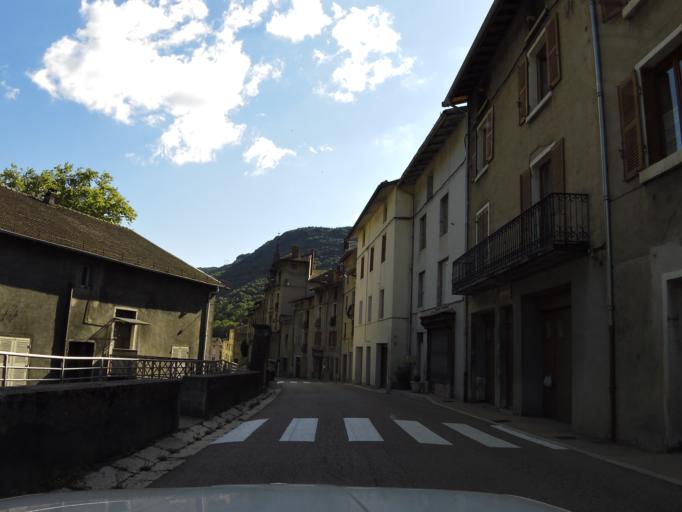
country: FR
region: Rhone-Alpes
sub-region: Departement de l'Ain
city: Tenay
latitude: 45.9206
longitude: 5.5096
